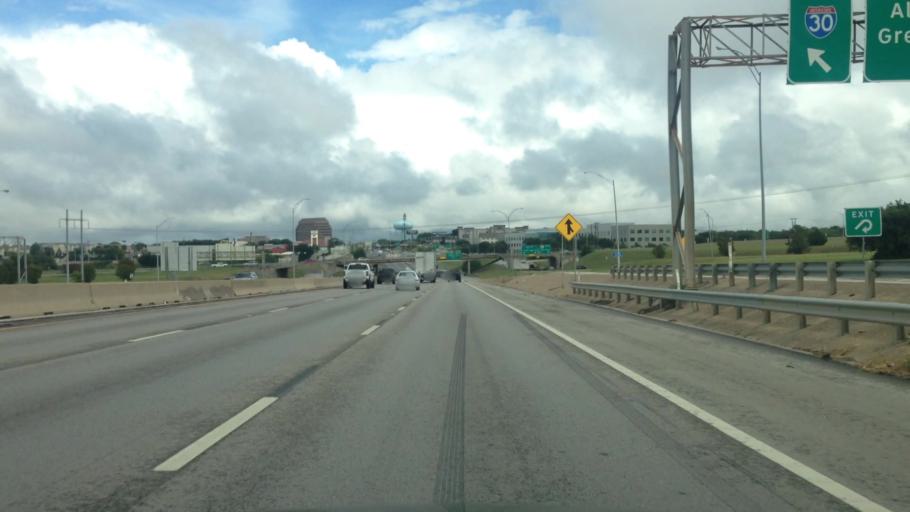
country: US
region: Texas
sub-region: Tarrant County
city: White Settlement
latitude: 32.7374
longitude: -97.4448
